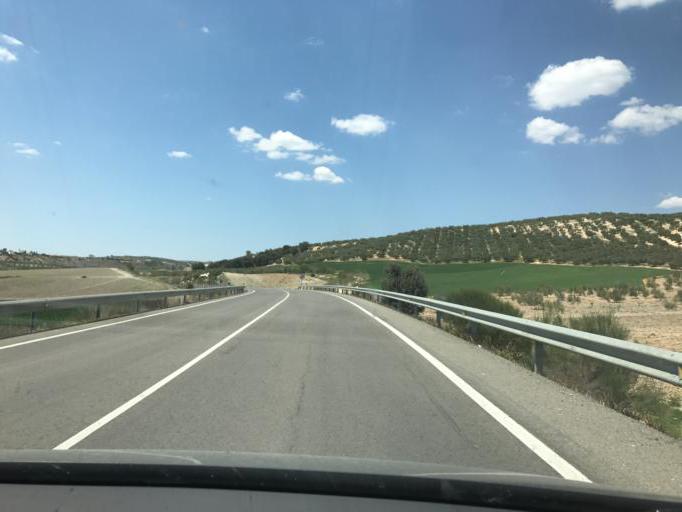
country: ES
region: Andalusia
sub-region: Provincia de Jaen
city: Frailes
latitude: 37.4424
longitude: -3.8546
